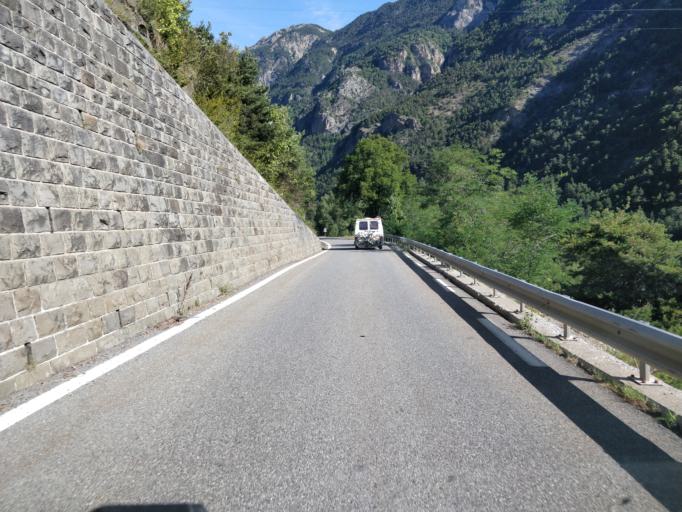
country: FR
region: Provence-Alpes-Cote d'Azur
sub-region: Departement des Alpes-de-Haute-Provence
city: Seyne-les-Alpes
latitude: 44.4141
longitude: 6.4480
